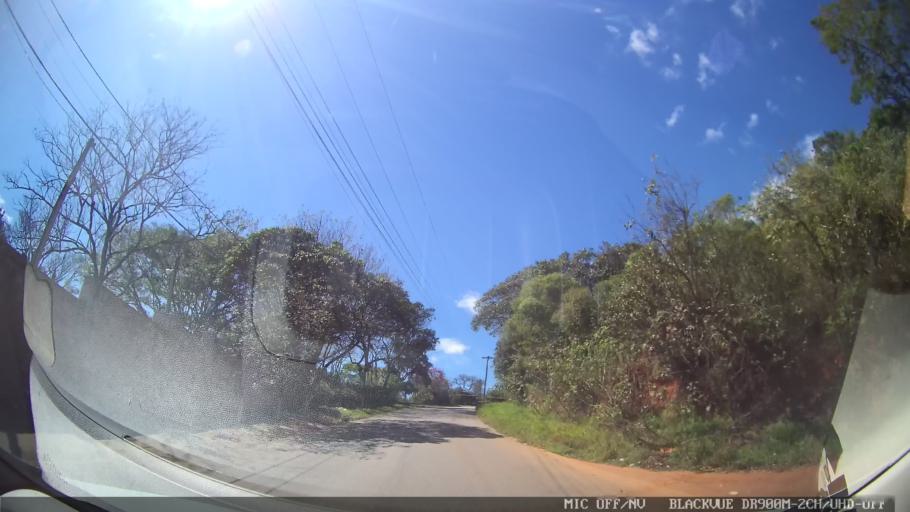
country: BR
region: Sao Paulo
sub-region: Jarinu
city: Jarinu
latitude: -23.1578
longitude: -46.7267
